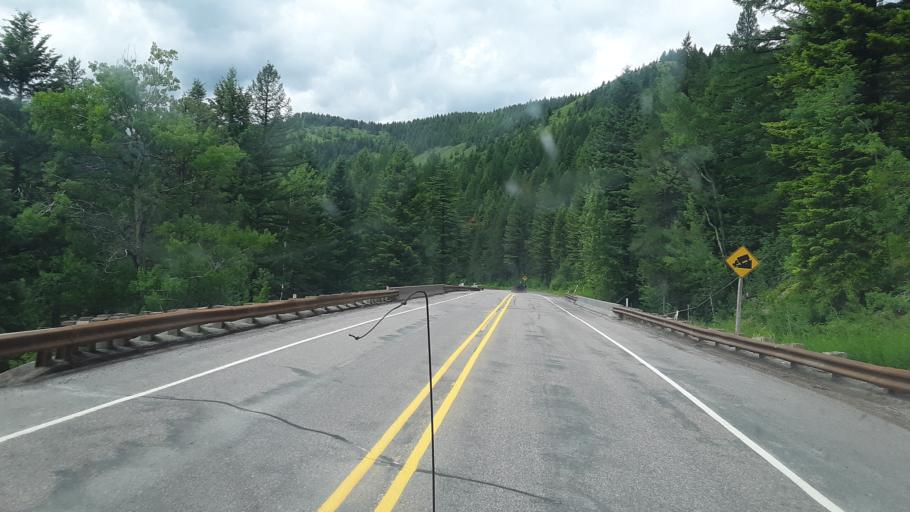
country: US
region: Montana
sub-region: Flathead County
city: Bigfork
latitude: 48.2618
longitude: -113.5765
